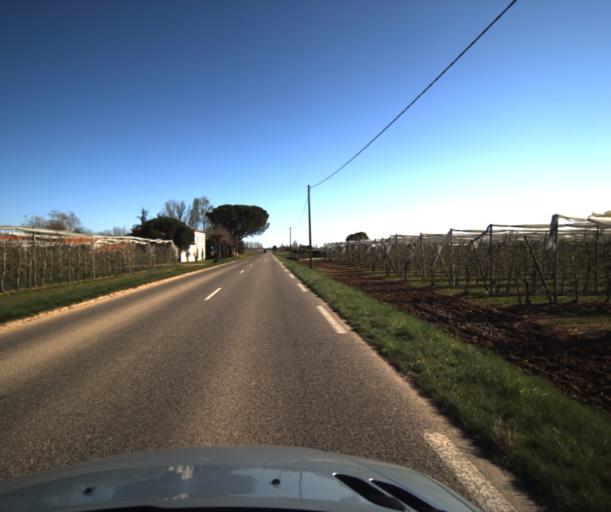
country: FR
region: Midi-Pyrenees
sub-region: Departement du Tarn-et-Garonne
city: Corbarieu
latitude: 43.9453
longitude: 1.3529
